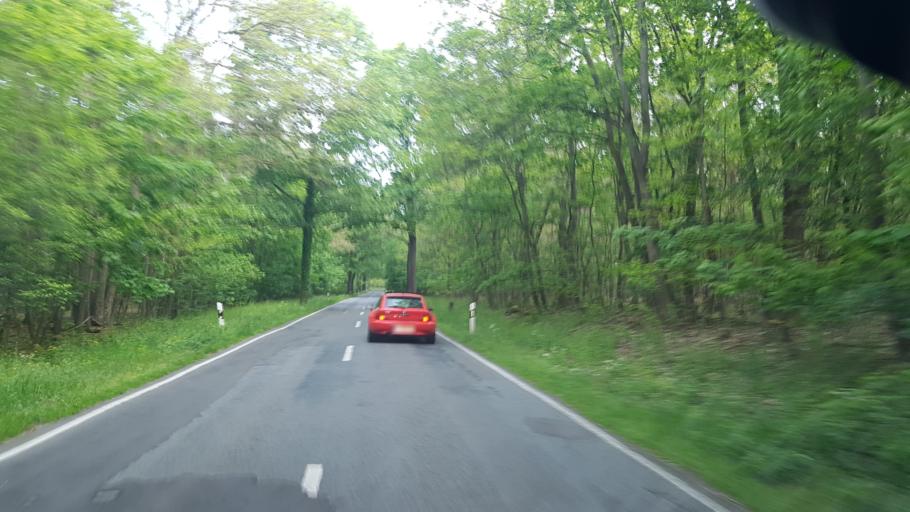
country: DE
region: Brandenburg
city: Baruth
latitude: 52.0175
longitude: 13.4699
